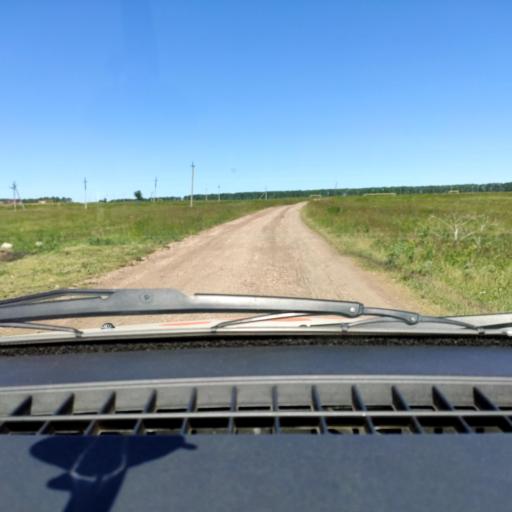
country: RU
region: Bashkortostan
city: Avdon
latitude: 54.5079
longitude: 55.7913
